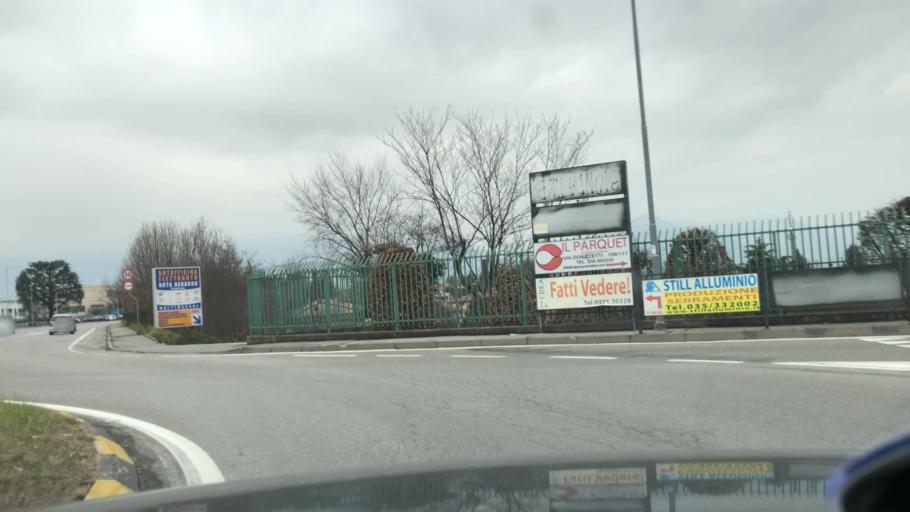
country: IT
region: Lombardy
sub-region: Provincia di Bergamo
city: Ponte San Pietro
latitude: 45.7083
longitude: 9.5838
